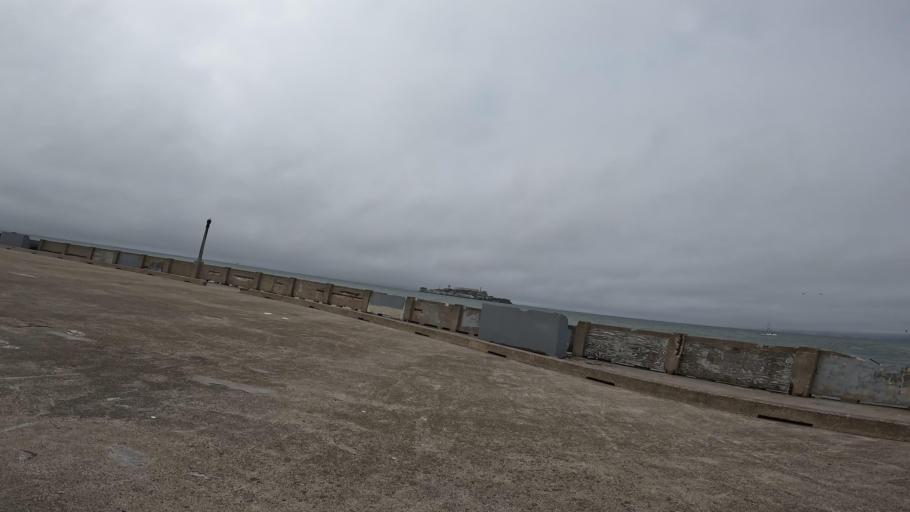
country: US
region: California
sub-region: San Francisco County
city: San Francisco
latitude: 37.8108
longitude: -122.4248
